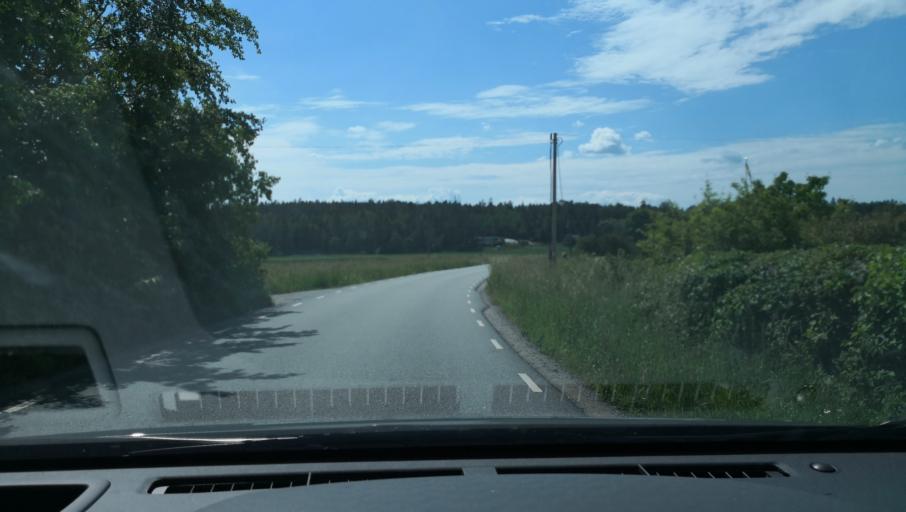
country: SE
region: Uppsala
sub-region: Habo Kommun
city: Balsta
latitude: 59.6709
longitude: 17.4625
